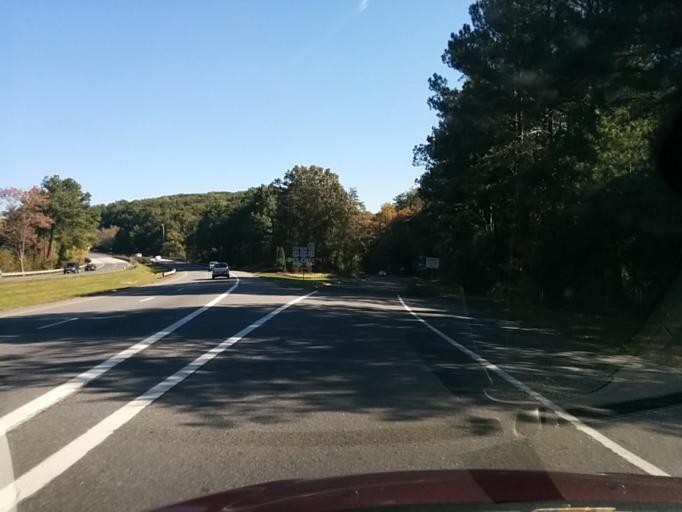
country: US
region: Virginia
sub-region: City of Charlottesville
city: Charlottesville
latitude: 38.0246
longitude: -78.5299
